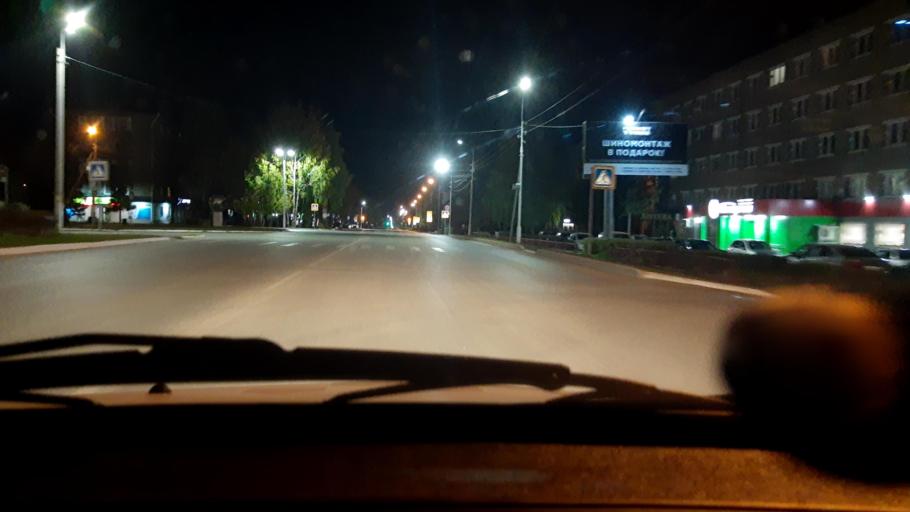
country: RU
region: Bashkortostan
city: Belebey
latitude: 54.0993
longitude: 54.1055
